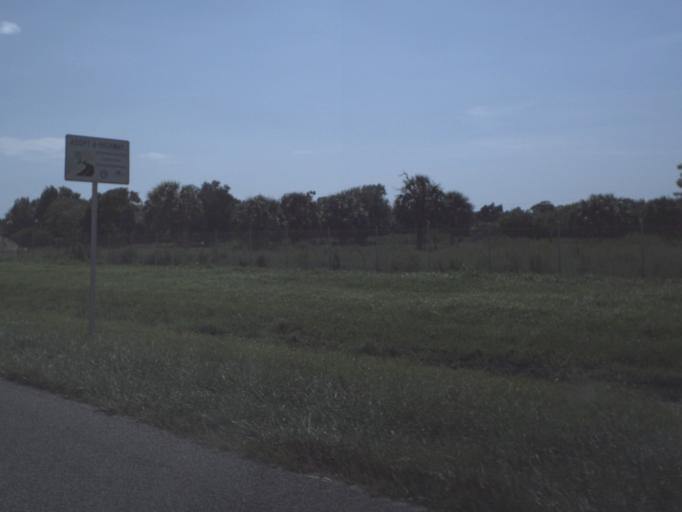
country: US
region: Florida
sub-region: Sarasota County
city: North Sarasota
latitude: 27.4005
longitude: -82.5331
